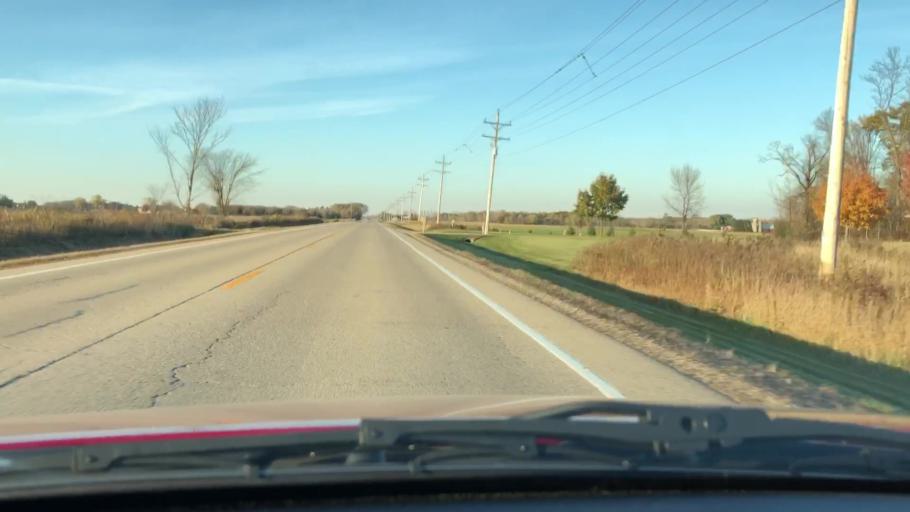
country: US
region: Wisconsin
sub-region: Outagamie County
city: Seymour
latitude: 44.4635
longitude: -88.2911
